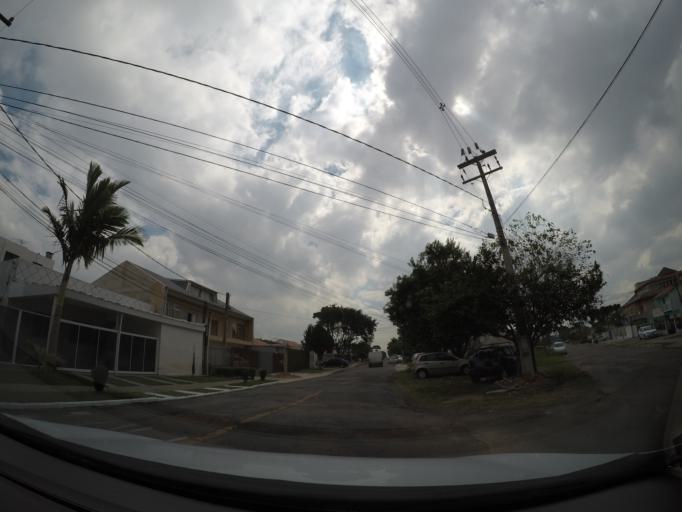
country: BR
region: Parana
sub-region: Sao Jose Dos Pinhais
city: Sao Jose dos Pinhais
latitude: -25.5007
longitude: -49.2476
